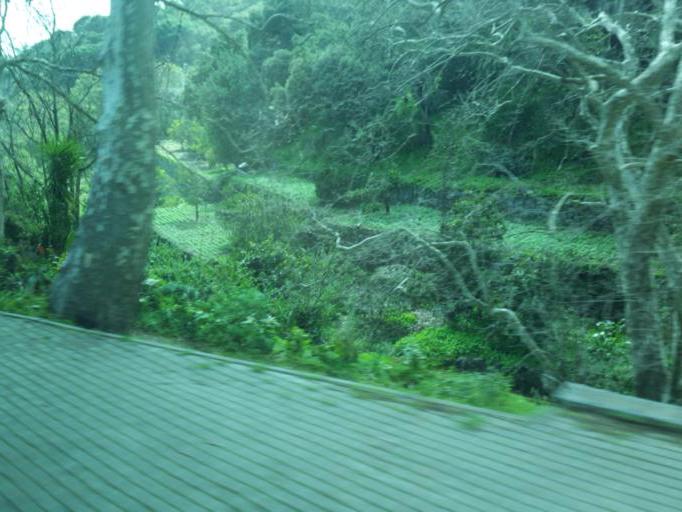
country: PT
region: Faro
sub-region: Monchique
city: Monchique
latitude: 37.2890
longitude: -8.5543
